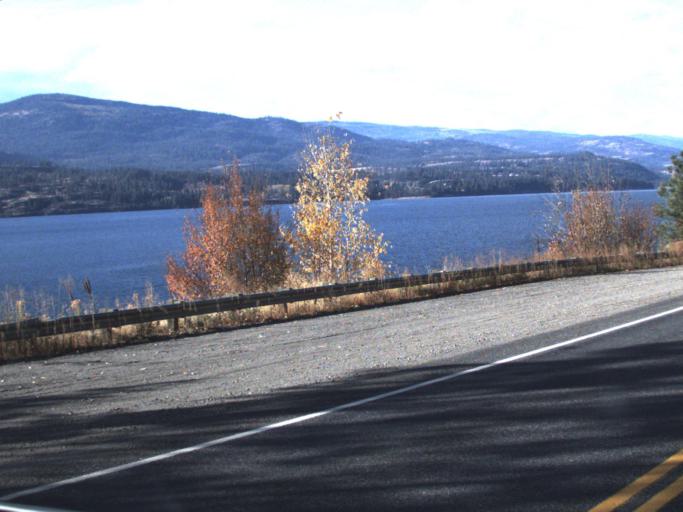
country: US
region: Washington
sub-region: Stevens County
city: Kettle Falls
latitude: 48.6369
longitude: -118.0812
